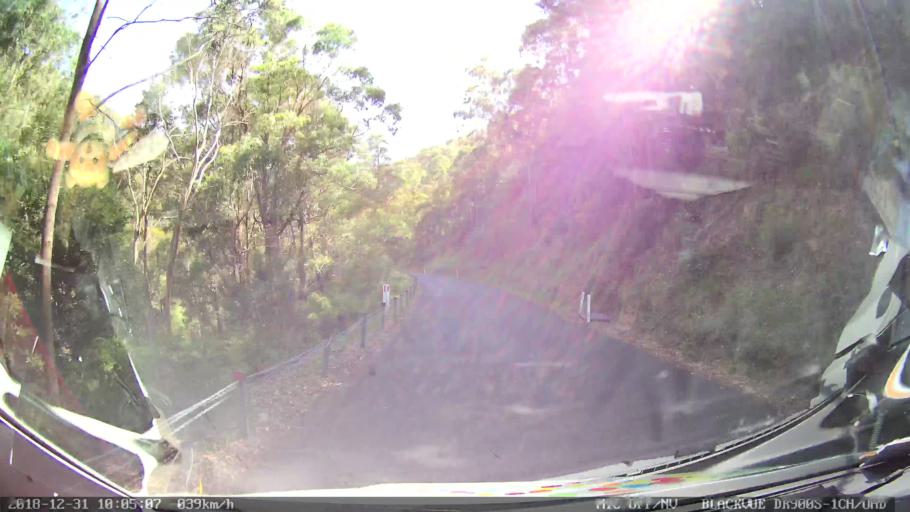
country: AU
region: New South Wales
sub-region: Snowy River
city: Jindabyne
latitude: -36.5279
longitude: 148.1936
